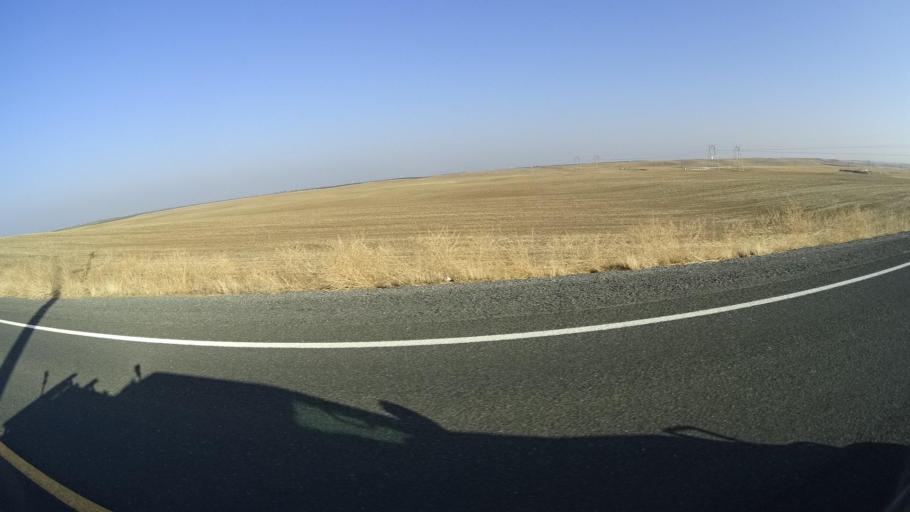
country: US
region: California
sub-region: Tulare County
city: Richgrove
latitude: 35.7619
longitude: -119.0664
